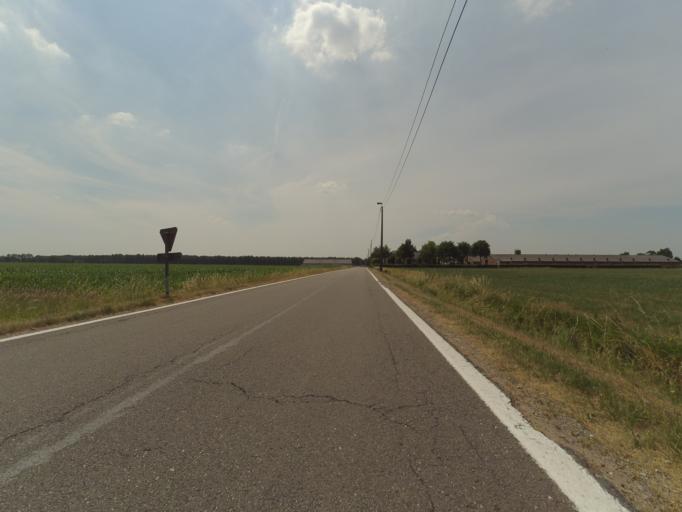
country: BE
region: Flanders
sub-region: Provincie Antwerpen
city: Kalmthout
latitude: 51.4141
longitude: 4.5260
